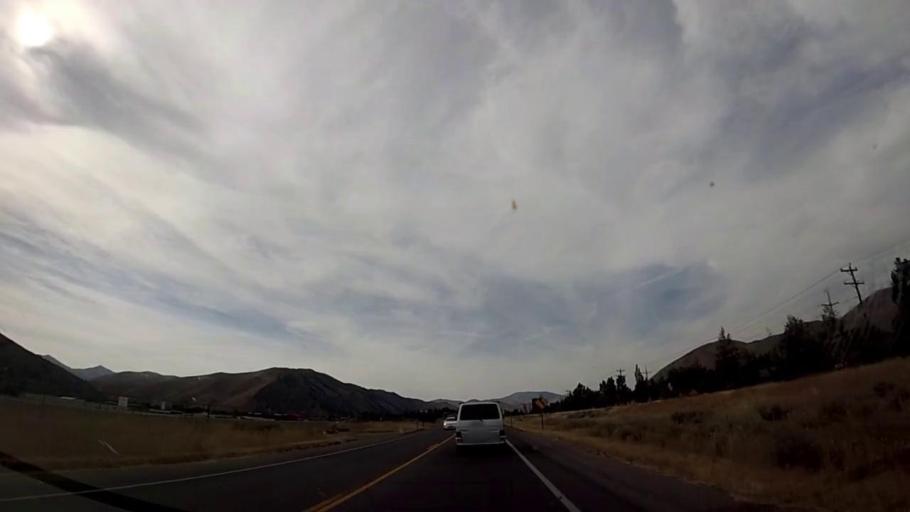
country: US
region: Idaho
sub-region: Blaine County
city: Hailey
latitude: 43.5101
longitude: -114.2999
